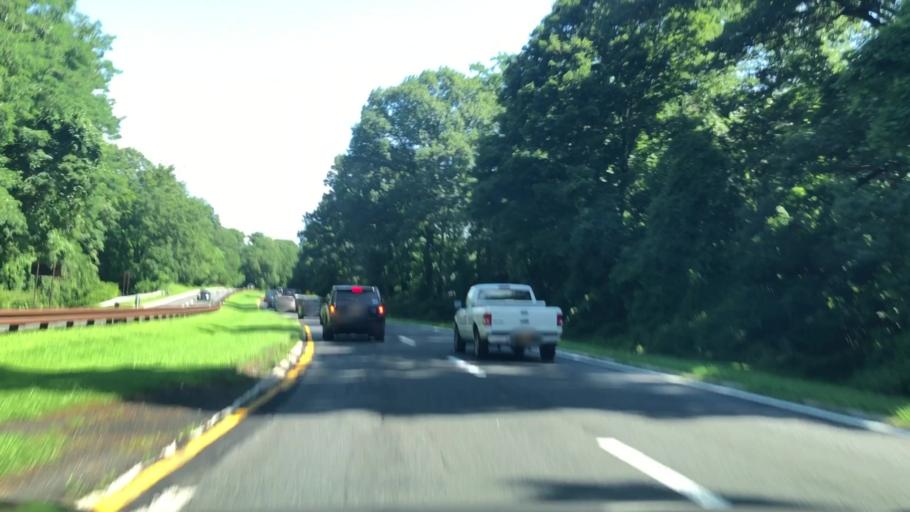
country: US
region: New York
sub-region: Westchester County
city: Greenville
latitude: 40.9951
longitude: -73.8052
